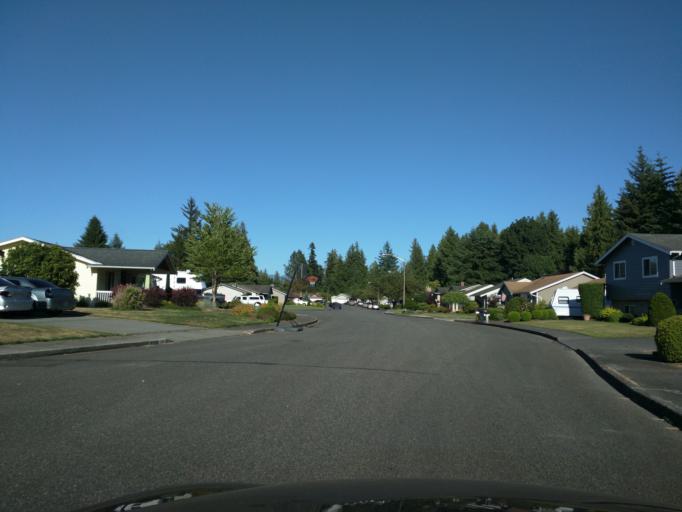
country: US
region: Washington
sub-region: Whatcom County
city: Lynden
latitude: 48.9531
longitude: -122.4506
